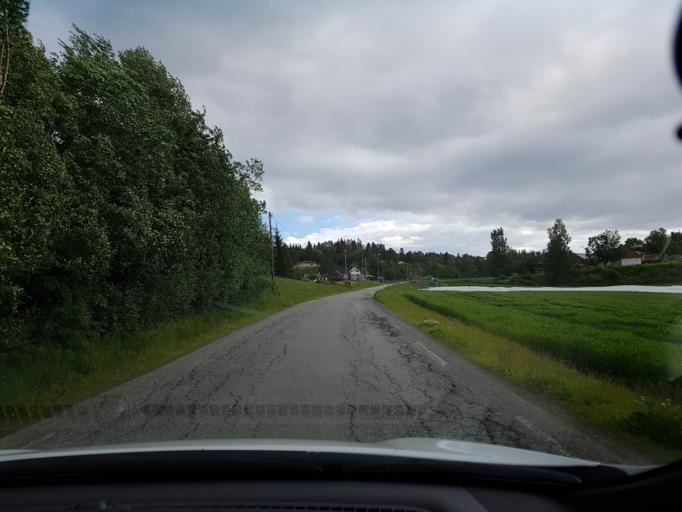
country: NO
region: Nord-Trondelag
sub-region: Frosta
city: Frosta
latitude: 63.6250
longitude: 10.7646
